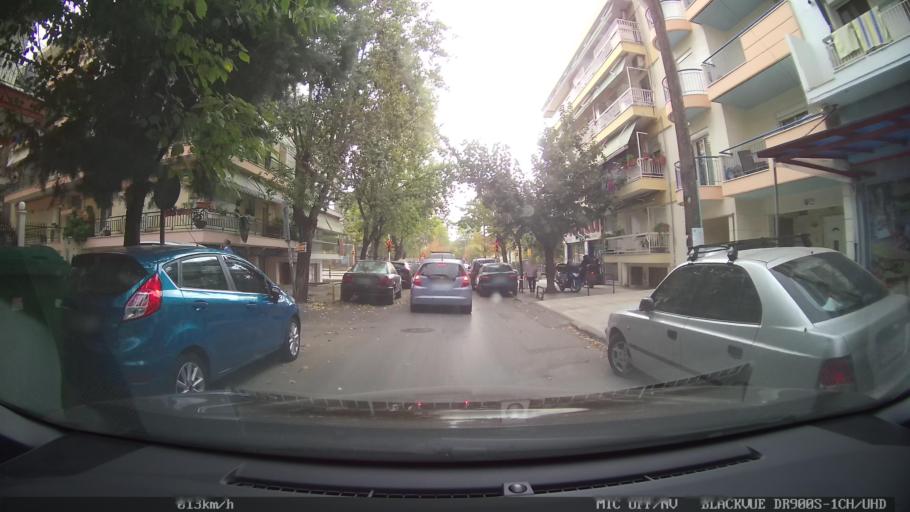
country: GR
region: Central Macedonia
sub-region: Nomos Thessalonikis
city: Triandria
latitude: 40.6114
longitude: 22.9720
